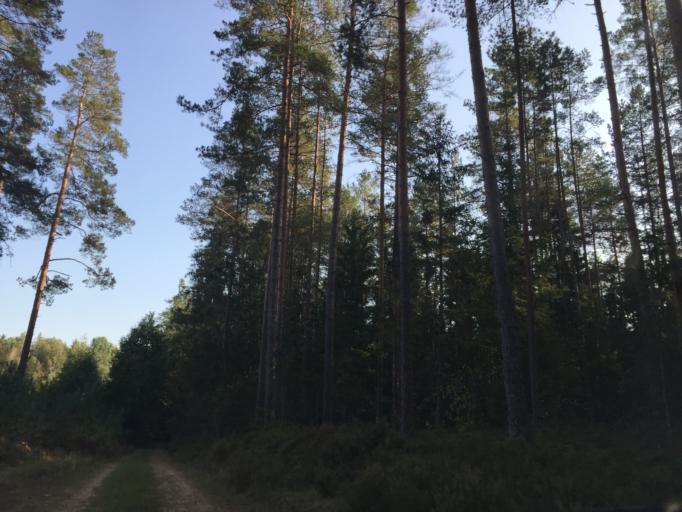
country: LV
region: Ogre
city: Ogre
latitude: 56.8444
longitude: 24.5835
